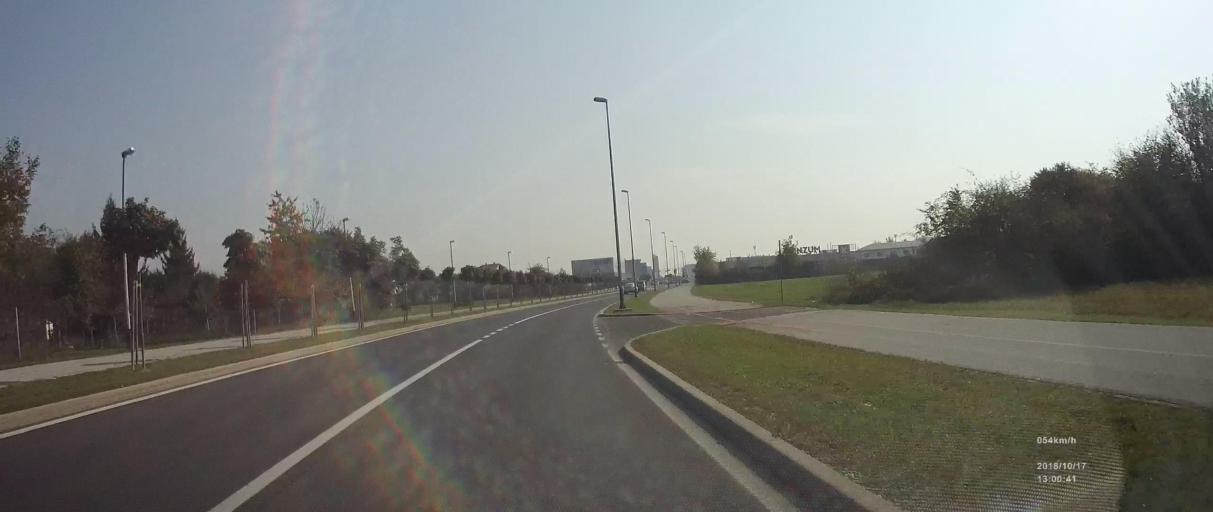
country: HR
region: Zagrebacka
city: Gradici
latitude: 45.7143
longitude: 16.0564
